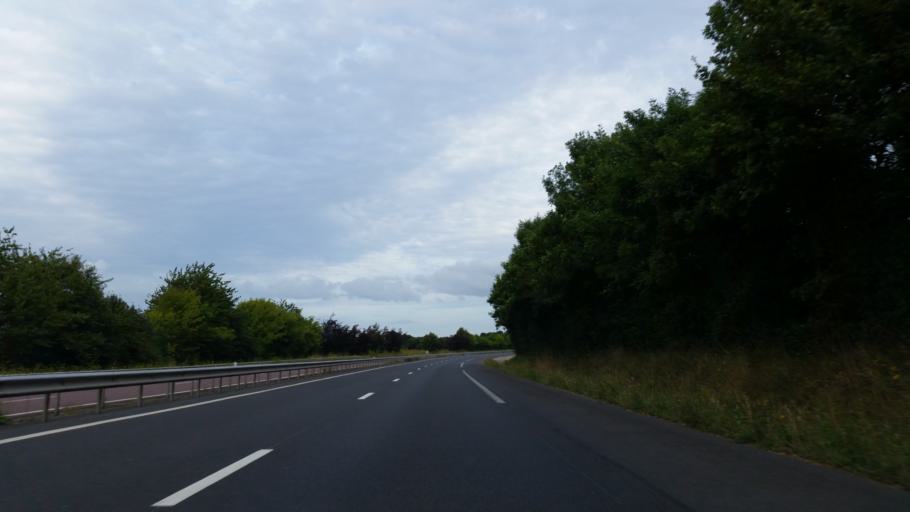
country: FR
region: Lower Normandy
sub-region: Departement du Calvados
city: Grandcamp-Maisy
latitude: 49.3433
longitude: -1.0302
